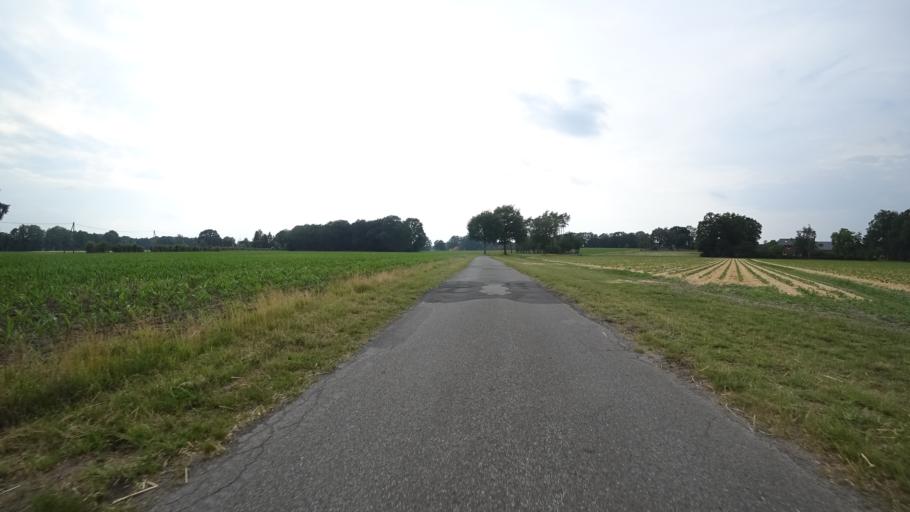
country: DE
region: North Rhine-Westphalia
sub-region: Regierungsbezirk Detmold
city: Guetersloh
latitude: 51.9493
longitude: 8.3728
